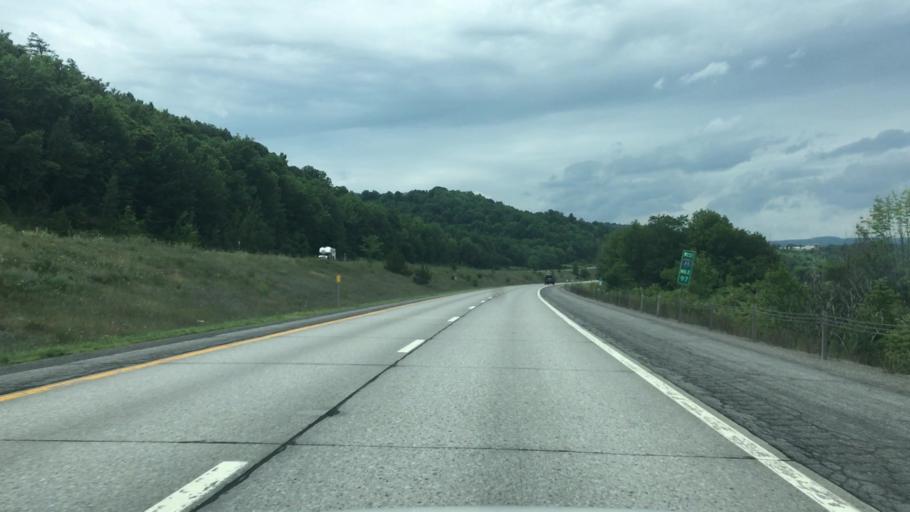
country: US
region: New York
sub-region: Schoharie County
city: Schoharie
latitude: 42.6806
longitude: -74.3770
